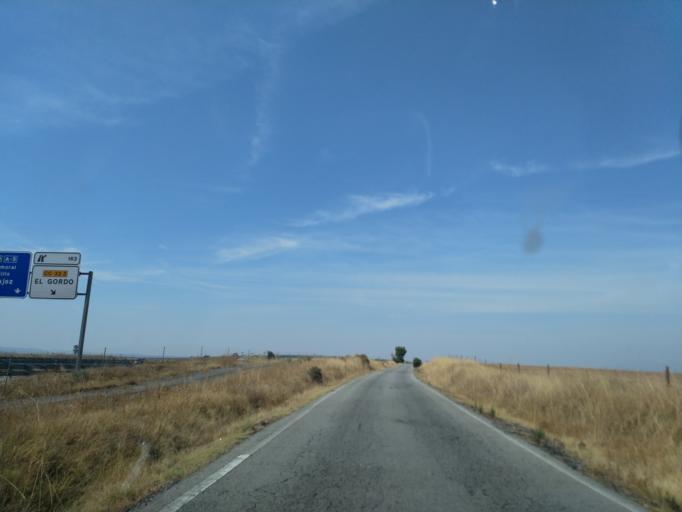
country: ES
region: Extremadura
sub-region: Provincia de Caceres
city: Berrocalejo
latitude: 39.8952
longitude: -5.3401
